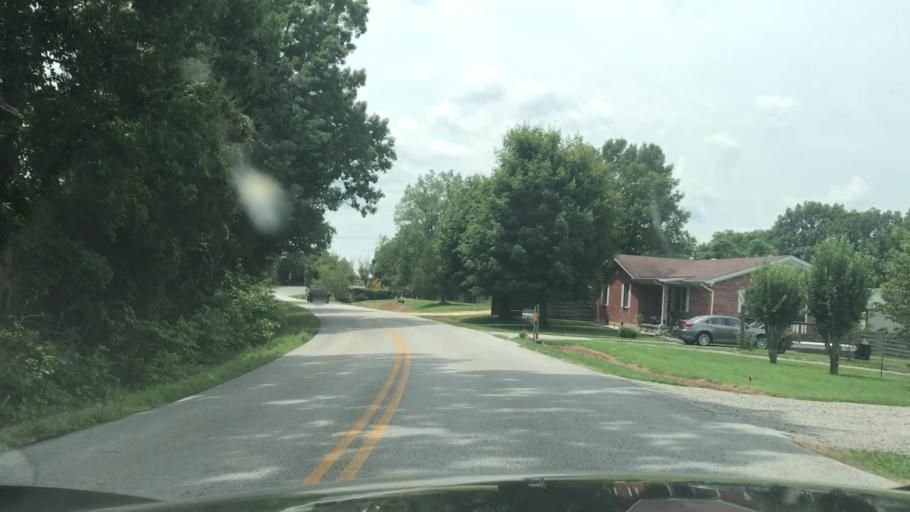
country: US
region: Kentucky
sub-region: Green County
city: Greensburg
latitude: 37.2707
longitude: -85.5316
